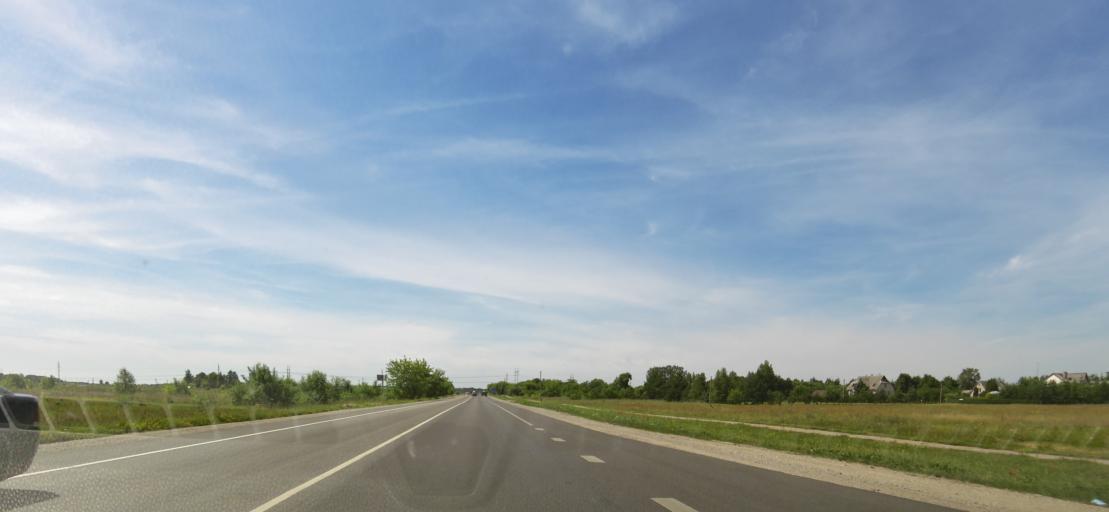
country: LT
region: Panevezys
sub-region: Panevezys City
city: Panevezys
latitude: 55.7323
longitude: 24.2916
